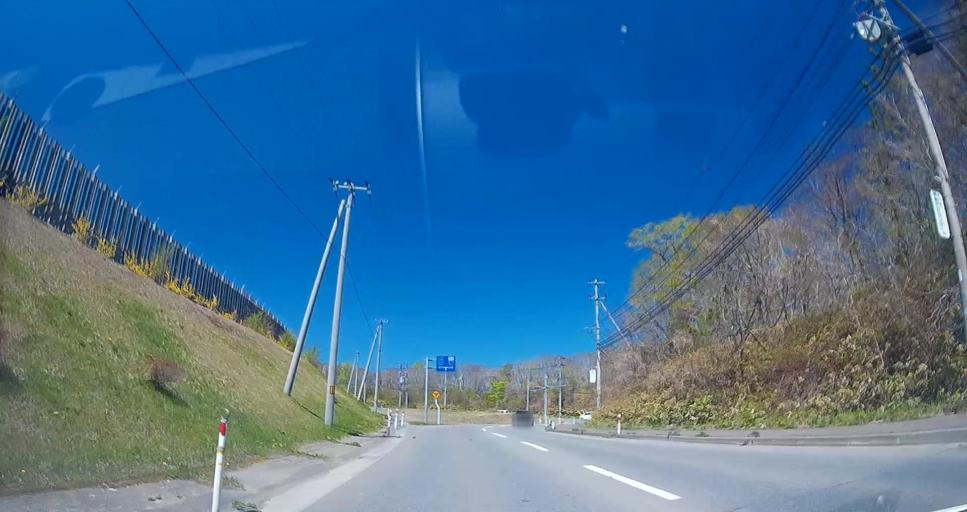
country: JP
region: Aomori
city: Misawa
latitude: 40.9801
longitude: 141.3585
